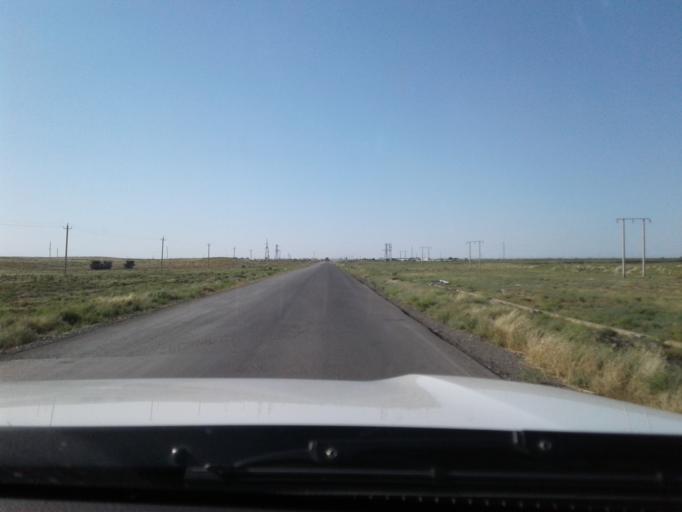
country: IR
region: Razavi Khorasan
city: Kalat-e Naderi
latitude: 37.1796
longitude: 60.0428
